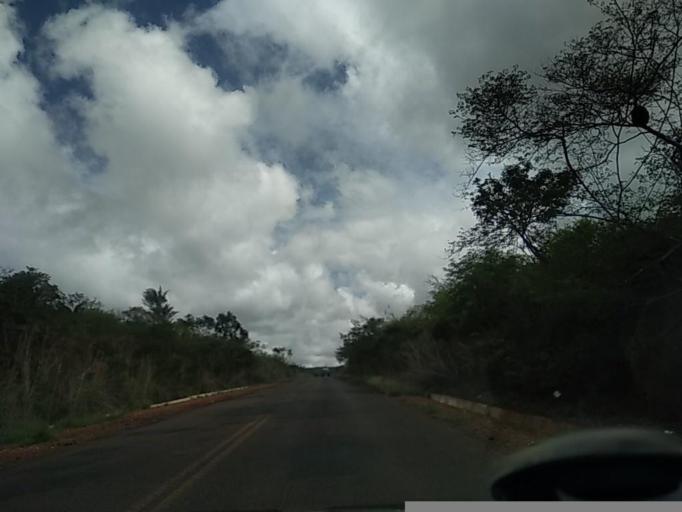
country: BR
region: Bahia
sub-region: Caetite
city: Caetite
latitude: -14.0364
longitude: -42.4866
